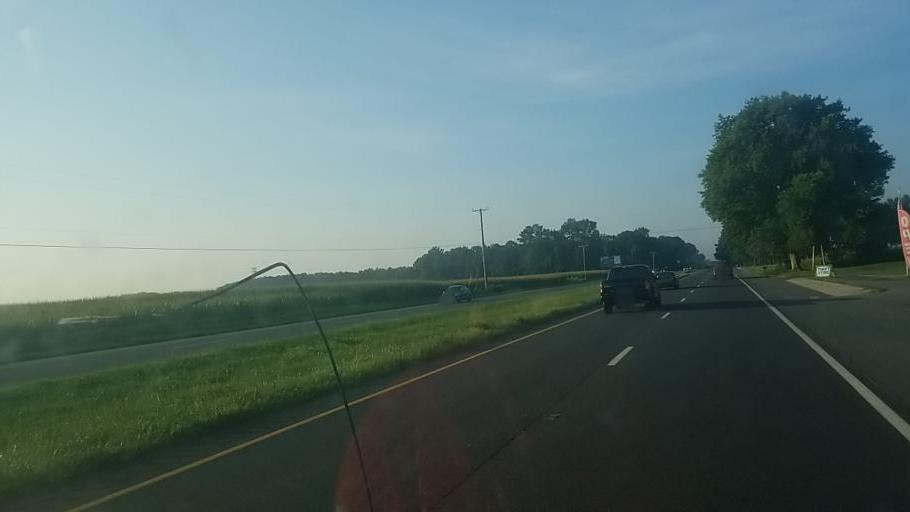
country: US
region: Delaware
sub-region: Sussex County
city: Selbyville
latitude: 38.4769
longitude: -75.2352
